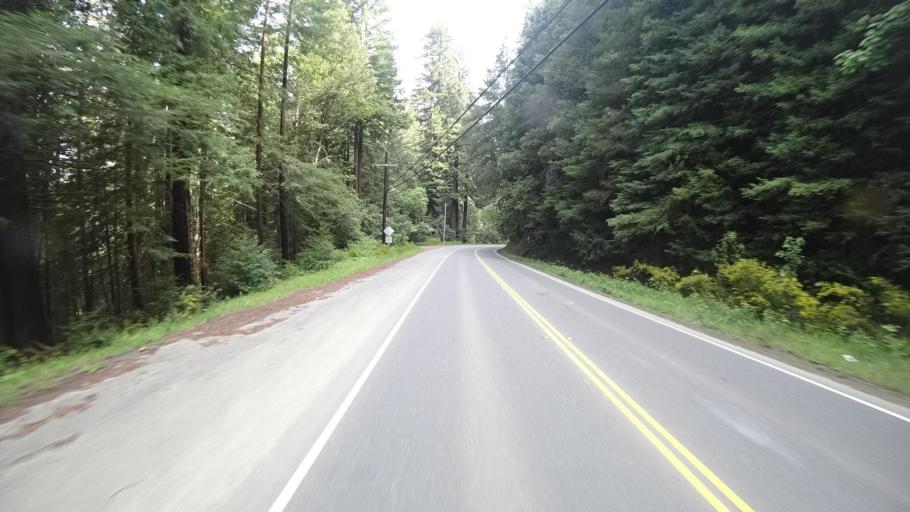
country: US
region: California
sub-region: Humboldt County
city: Redway
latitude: 40.1298
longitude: -123.8187
